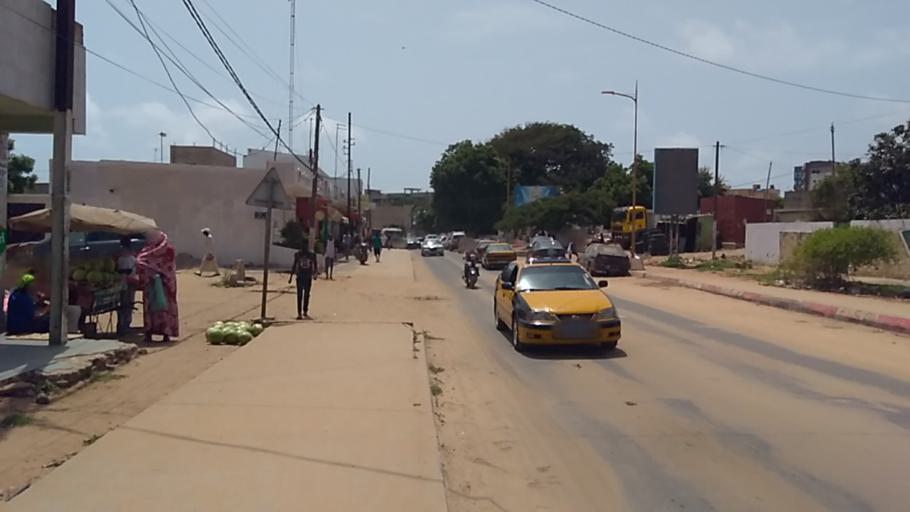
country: SN
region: Dakar
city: Mermoz Boabab
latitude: 14.7204
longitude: -17.4908
